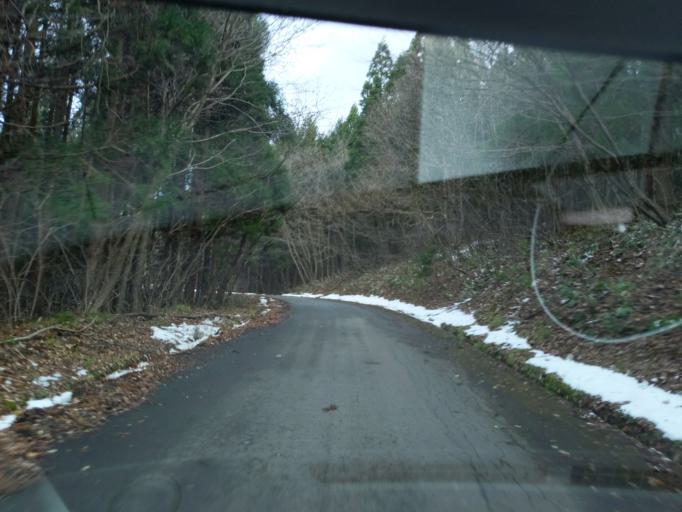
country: JP
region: Iwate
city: Ichinoseki
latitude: 38.9933
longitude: 140.9980
